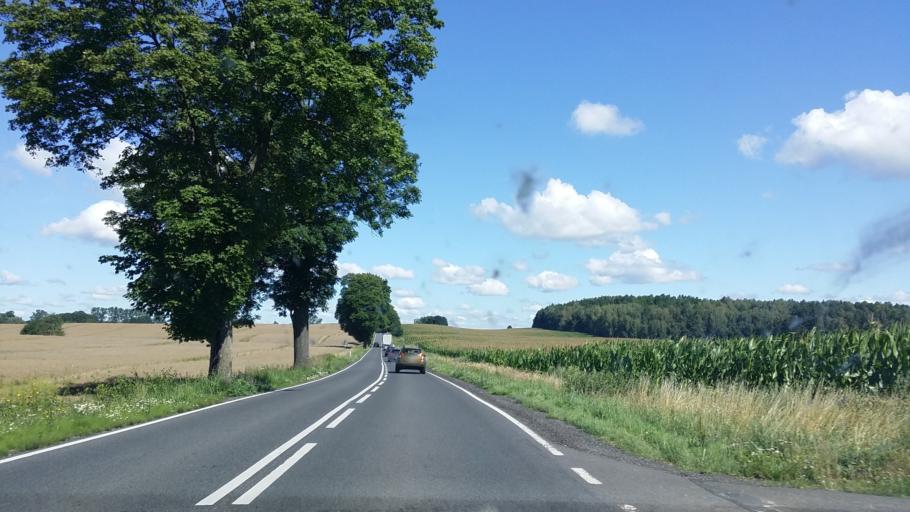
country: PL
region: West Pomeranian Voivodeship
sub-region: Powiat drawski
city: Kalisz Pomorski
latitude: 53.3143
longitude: 15.9075
